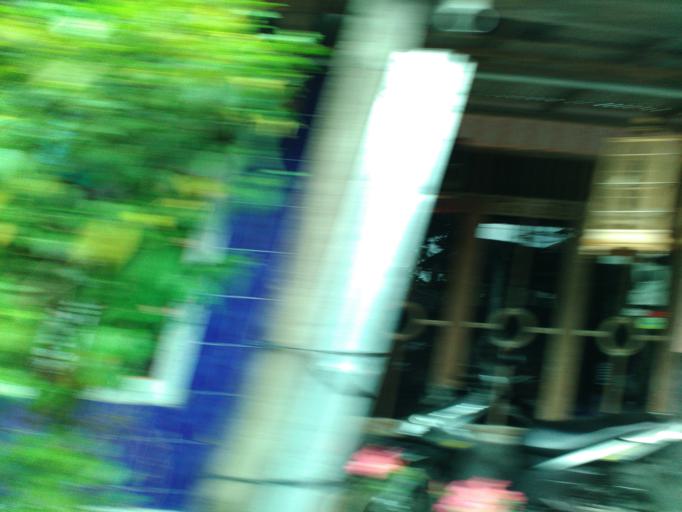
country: ID
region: Central Java
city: Gatak
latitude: -7.6049
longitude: 110.7009
